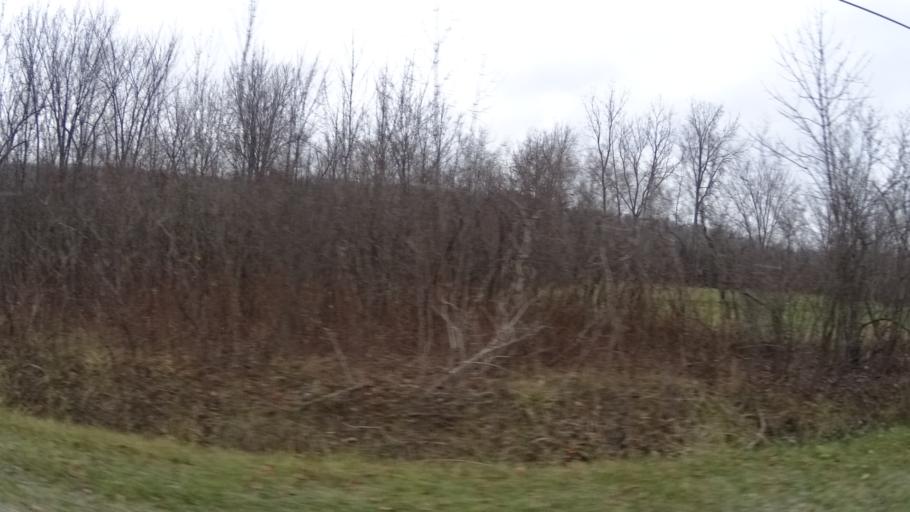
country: US
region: Ohio
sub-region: Lorain County
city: South Amherst
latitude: 41.3385
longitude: -82.2592
